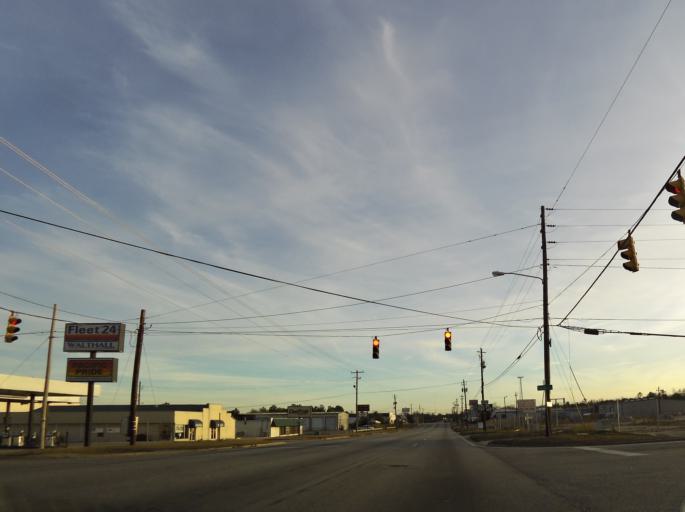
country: US
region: Georgia
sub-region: Bibb County
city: Macon
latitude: 32.8082
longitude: -83.6404
